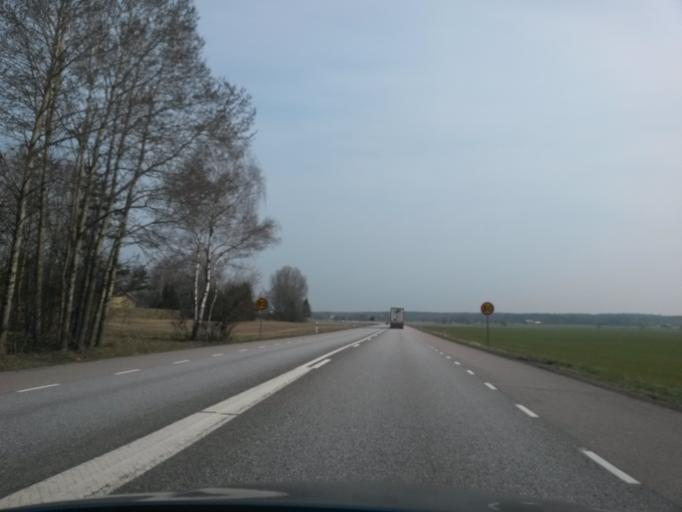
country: SE
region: Vaestra Goetaland
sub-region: Mariestads Kommun
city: Mariestad
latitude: 58.7380
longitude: 13.9329
